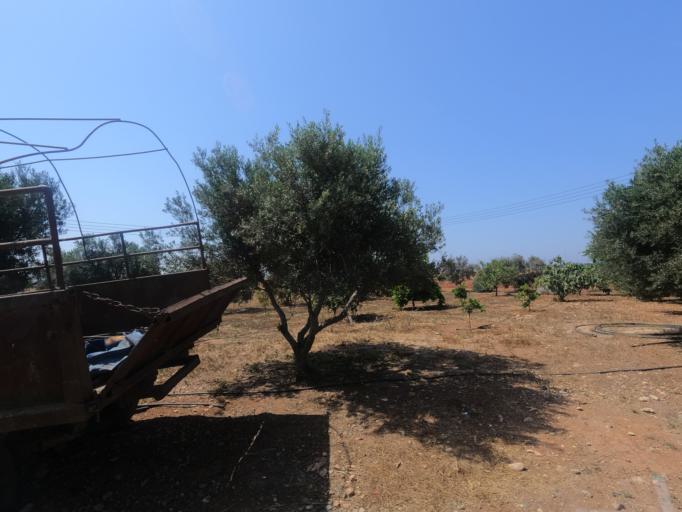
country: CY
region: Ammochostos
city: Avgorou
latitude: 35.0171
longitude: 33.8213
